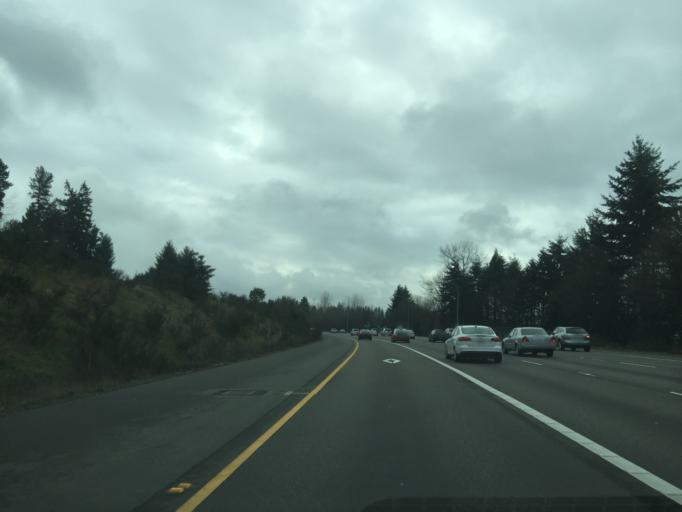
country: US
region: Washington
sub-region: Snohomish County
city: Mountlake Terrace
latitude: 47.8031
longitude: -122.3124
